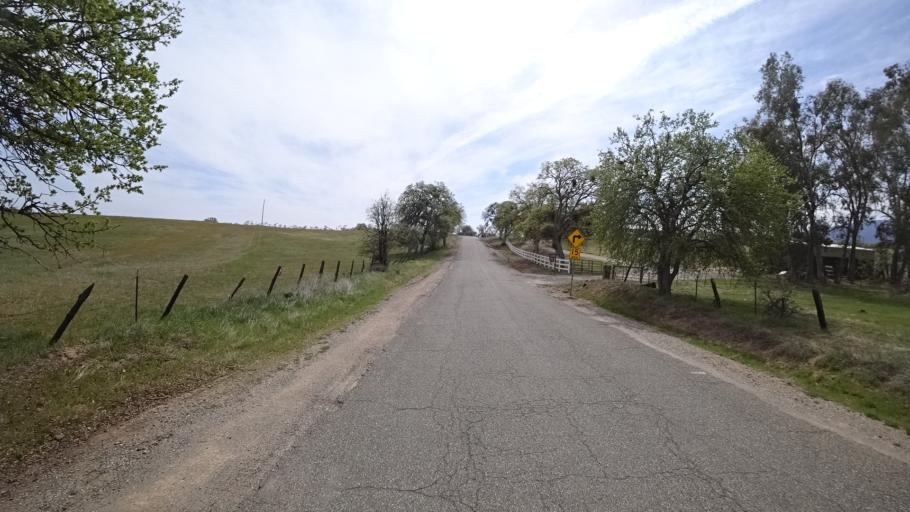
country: US
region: California
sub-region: Glenn County
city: Willows
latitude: 39.5932
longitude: -122.5539
